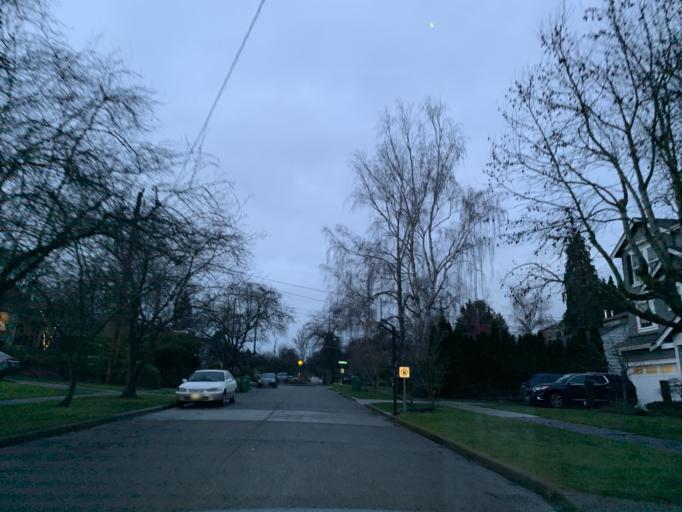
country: US
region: Washington
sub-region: King County
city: Yarrow Point
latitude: 47.6624
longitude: -122.2758
